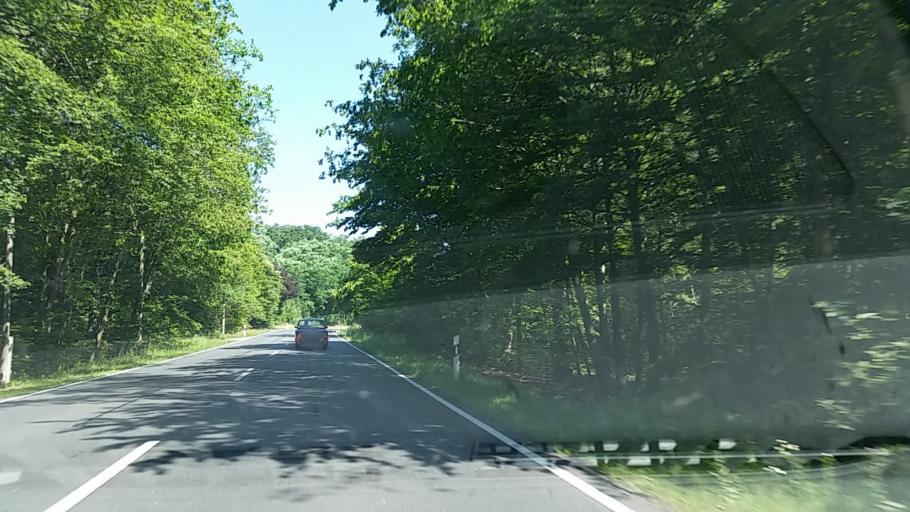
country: DE
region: Saxony-Anhalt
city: Kemberg
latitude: 51.6930
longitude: 12.6142
